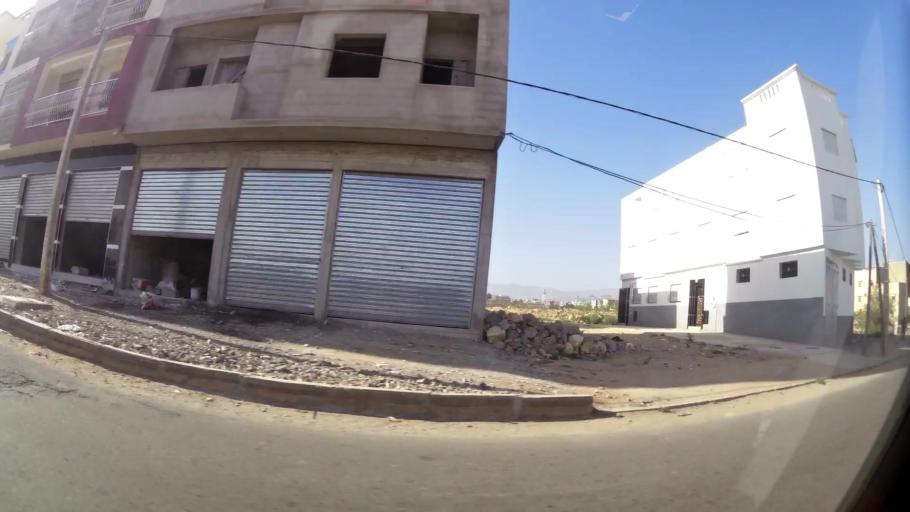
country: MA
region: Souss-Massa-Draa
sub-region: Inezgane-Ait Mellou
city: Inezgane
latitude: 30.3738
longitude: -9.5127
